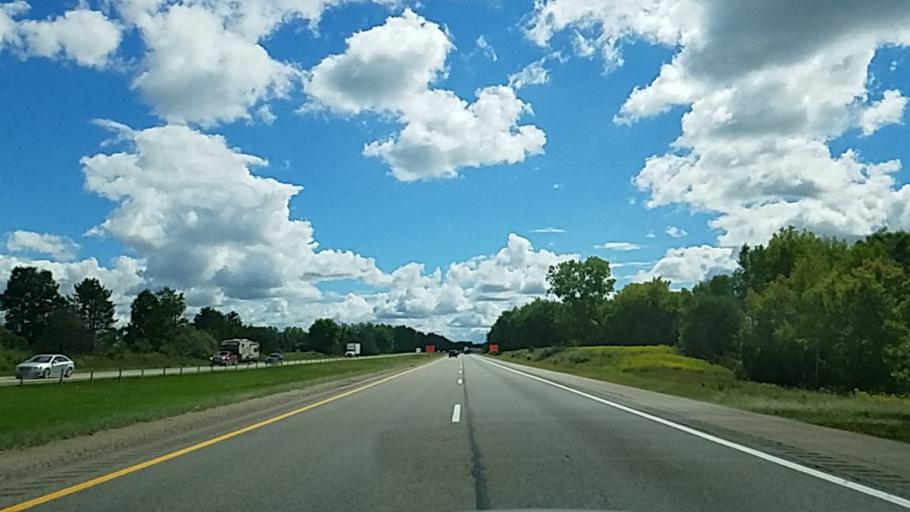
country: US
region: Michigan
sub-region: Livingston County
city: Brighton
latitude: 42.5897
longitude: -83.7396
